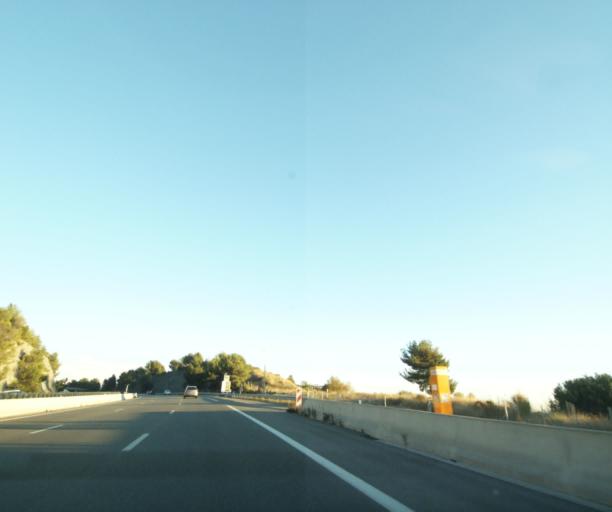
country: FR
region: Provence-Alpes-Cote d'Azur
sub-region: Departement des Bouches-du-Rhone
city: Ceyreste
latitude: 43.1927
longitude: 5.6524
